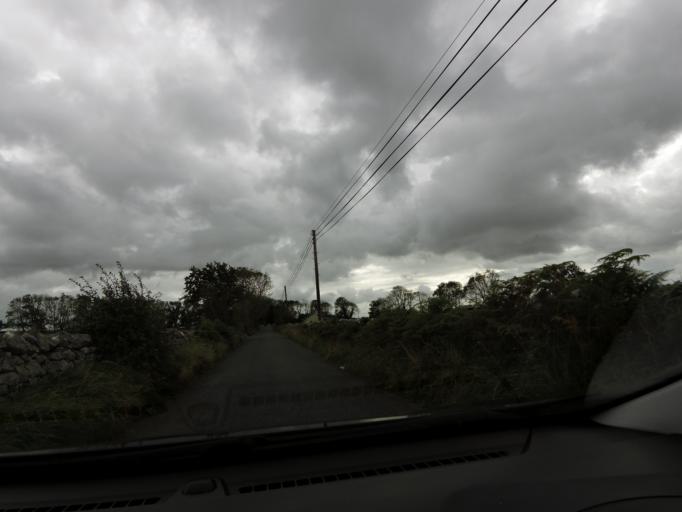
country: IE
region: Connaught
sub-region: County Galway
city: Athenry
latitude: 53.3228
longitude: -8.7827
